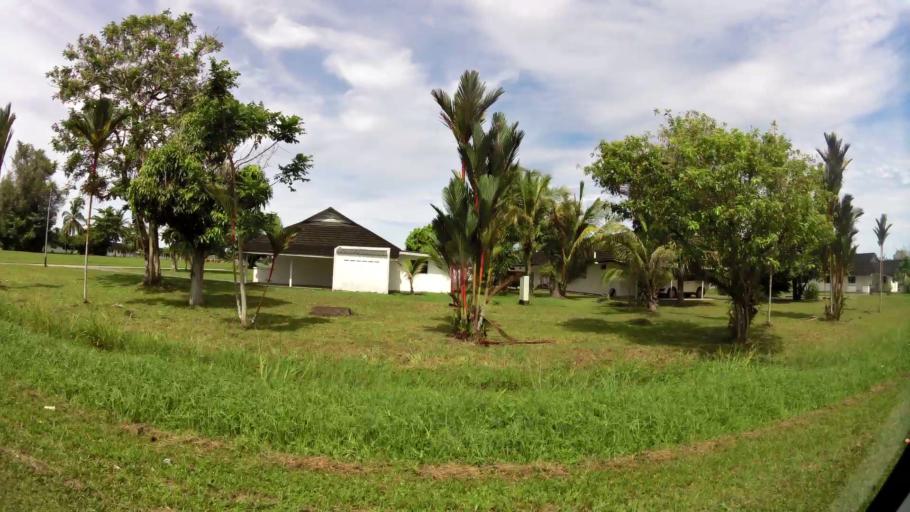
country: BN
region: Belait
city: Seria
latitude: 4.6110
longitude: 114.3232
